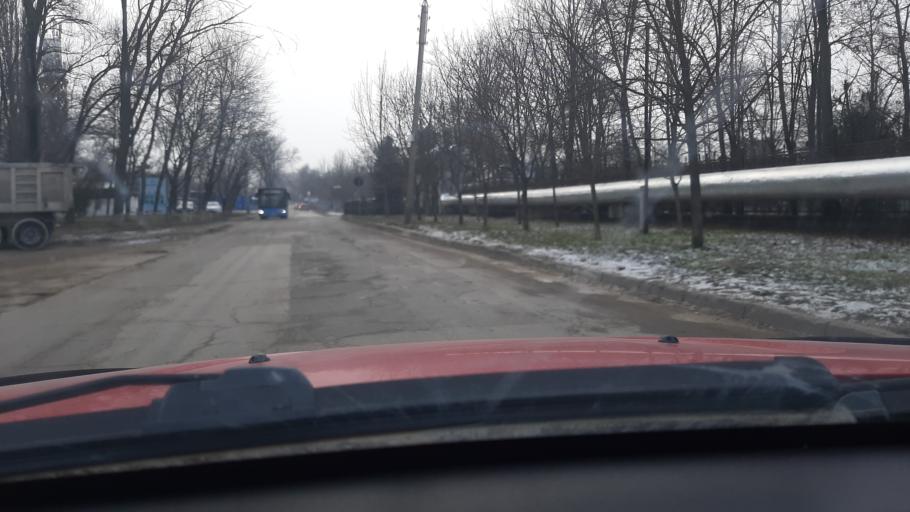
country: MD
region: Chisinau
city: Chisinau
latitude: 46.9755
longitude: 28.8940
